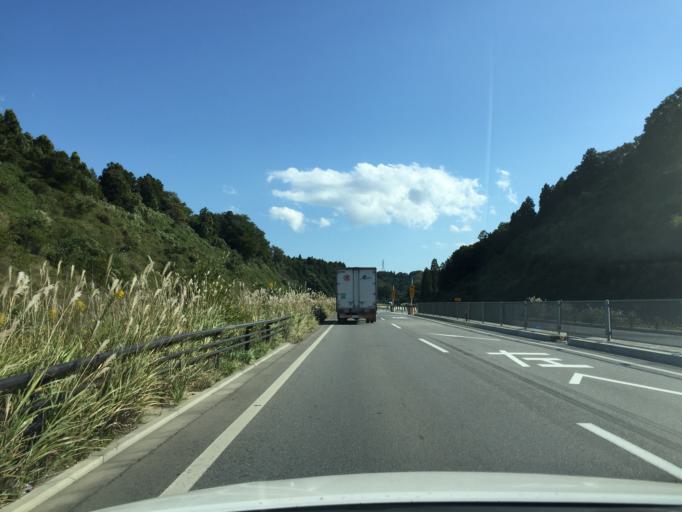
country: JP
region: Fukushima
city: Iwaki
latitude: 37.0439
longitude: 140.8736
